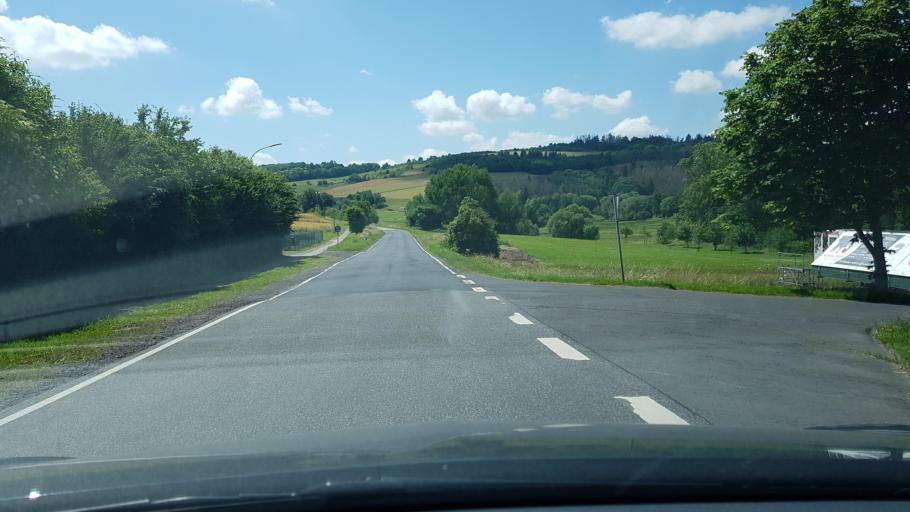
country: DE
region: Rheinland-Pfalz
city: Volkesfeld
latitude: 50.4007
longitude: 7.1406
